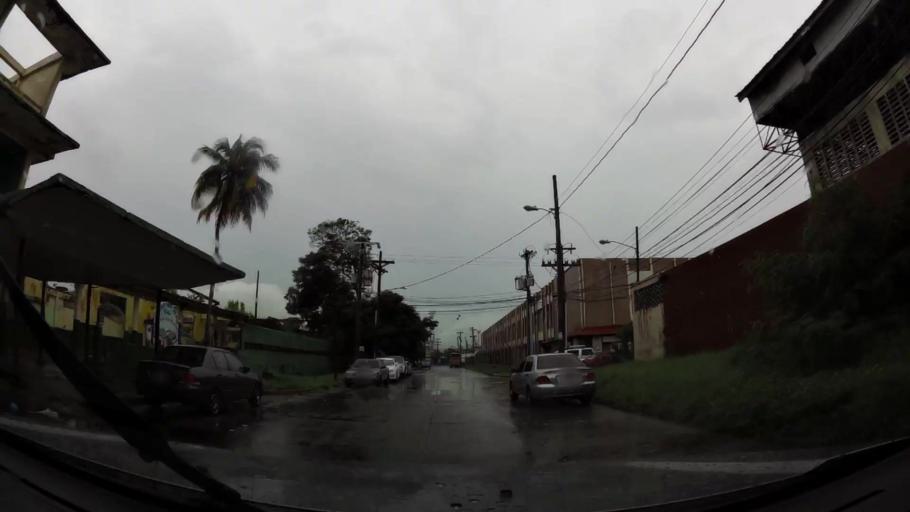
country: PA
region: Colon
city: Colon
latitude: 9.3569
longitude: -79.8937
